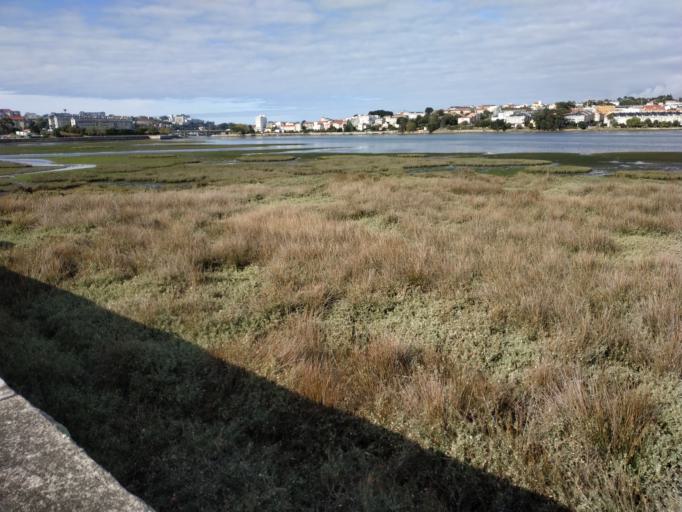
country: ES
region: Galicia
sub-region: Provincia da Coruna
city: Culleredo
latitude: 43.3230
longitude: -8.3754
